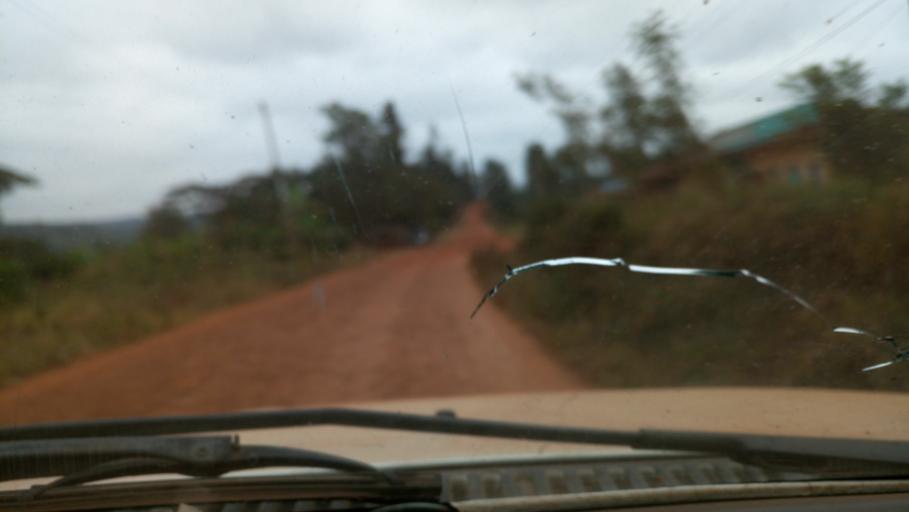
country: KE
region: Murang'a District
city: Maragua
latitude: -0.7720
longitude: 37.0496
